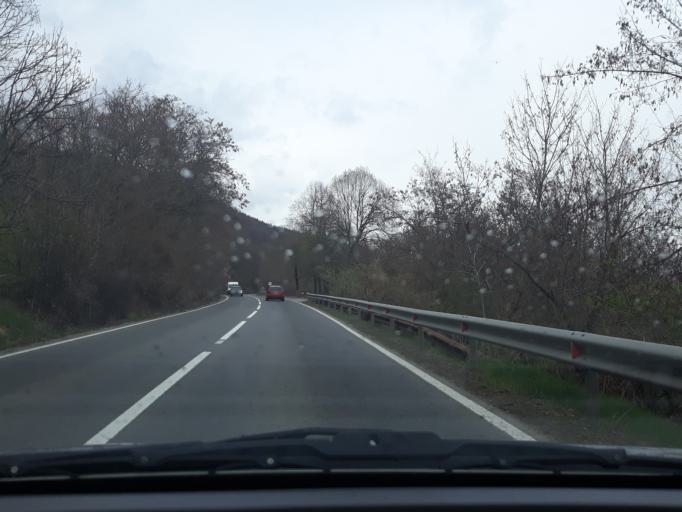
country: RO
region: Harghita
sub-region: Comuna Lupeni
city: Lupeni
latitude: 46.4129
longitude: 25.2236
